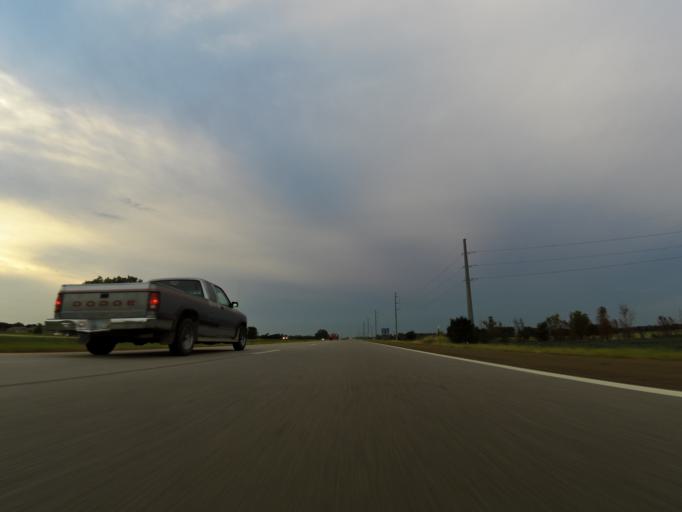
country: US
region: Kansas
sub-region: Sedgwick County
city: Maize
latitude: 37.7725
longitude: -97.4542
